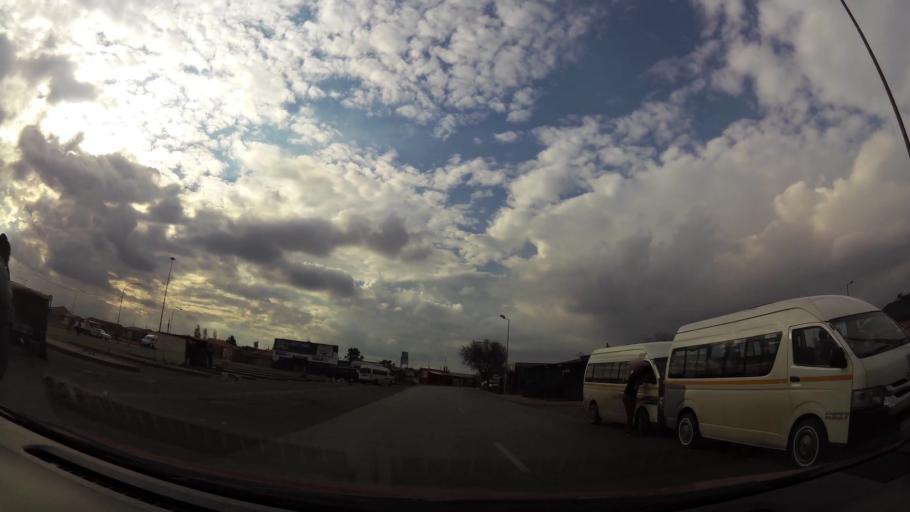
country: ZA
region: Gauteng
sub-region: City of Johannesburg Metropolitan Municipality
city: Soweto
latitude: -26.2473
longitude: 27.8183
